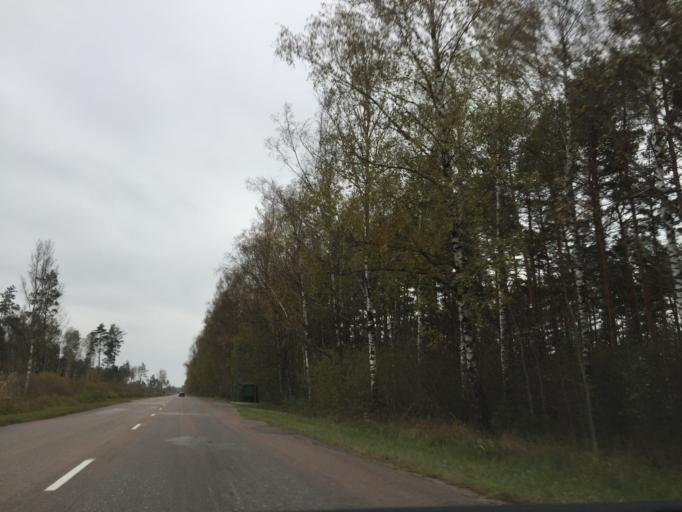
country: LV
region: Marupe
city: Marupe
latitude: 56.8698
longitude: 24.0631
